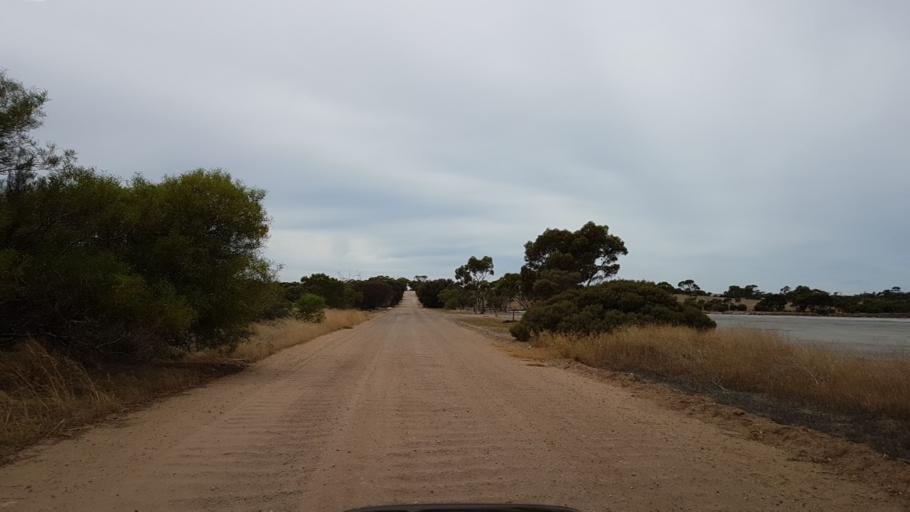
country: AU
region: South Australia
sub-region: Yorke Peninsula
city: Port Victoria
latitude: -34.7776
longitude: 137.5954
